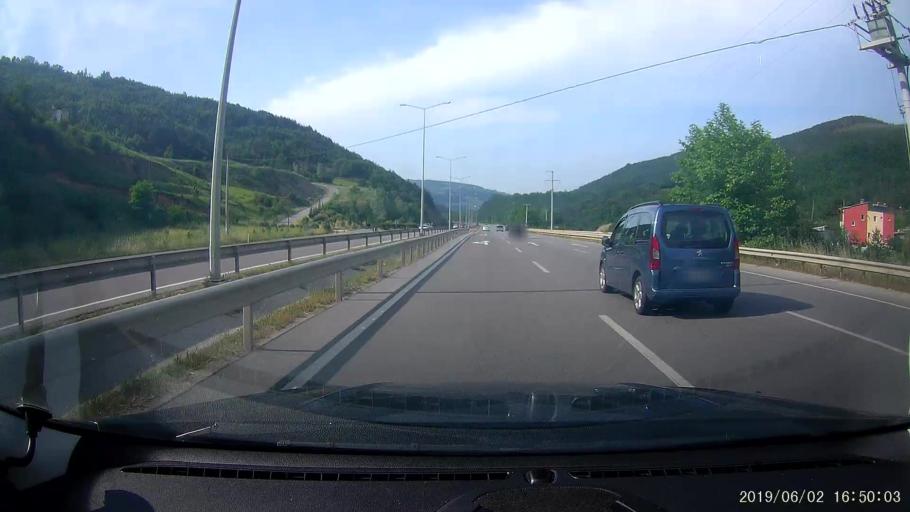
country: TR
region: Samsun
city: Samsun
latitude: 41.2467
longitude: 36.1727
